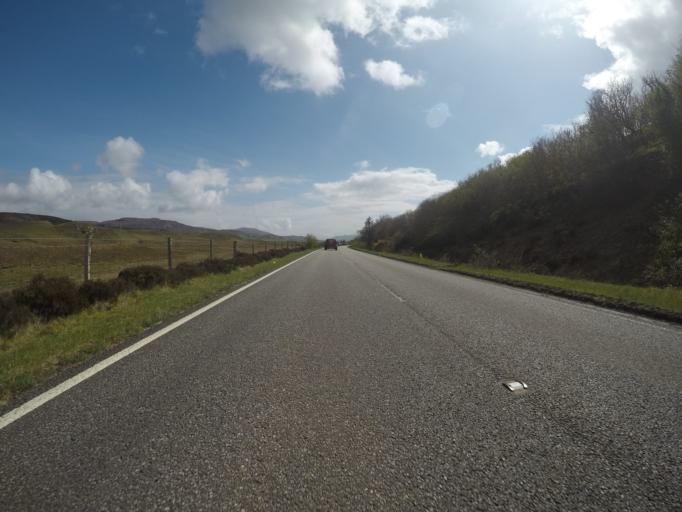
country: GB
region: Scotland
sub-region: Highland
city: Isle of Skye
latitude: 57.5087
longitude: -6.3376
